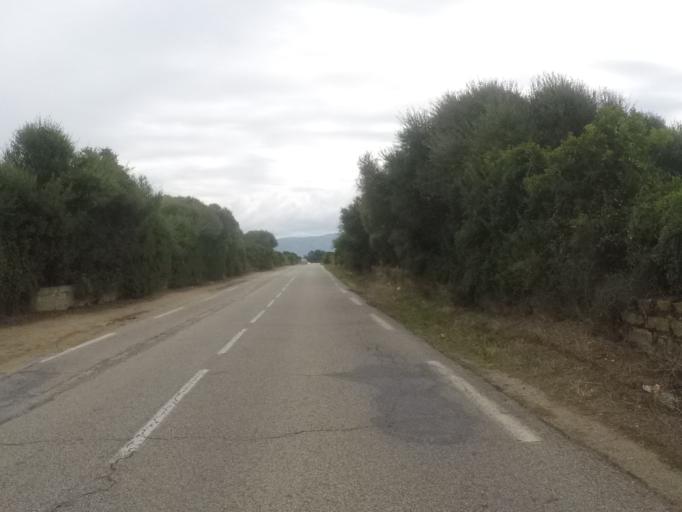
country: FR
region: Corsica
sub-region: Departement de la Corse-du-Sud
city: Propriano
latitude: 41.7080
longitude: 8.8306
